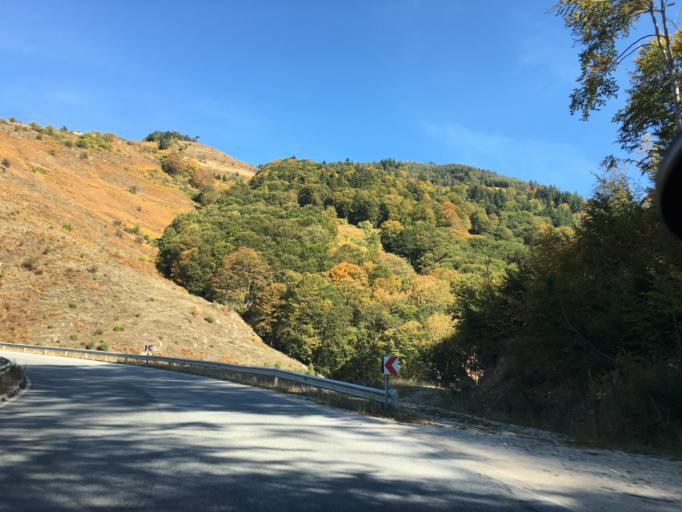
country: BG
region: Smolyan
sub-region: Obshtina Devin
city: Devin
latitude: 41.7866
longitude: 24.4713
